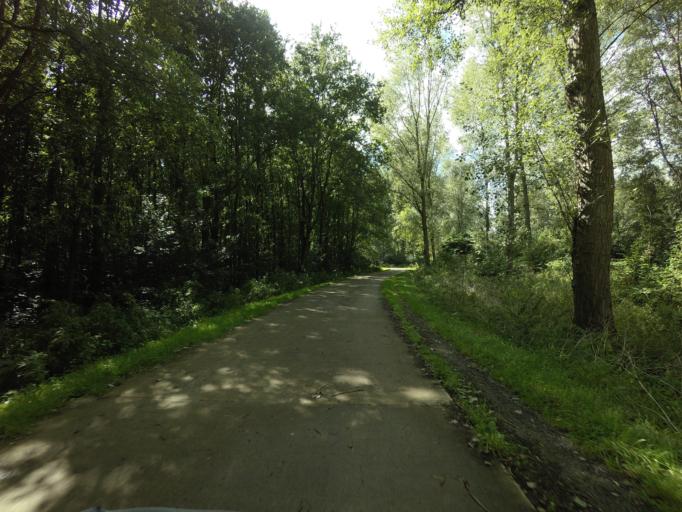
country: NL
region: North Holland
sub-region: Gemeente Purmerend
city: Purmerend
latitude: 52.4881
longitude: 4.9889
